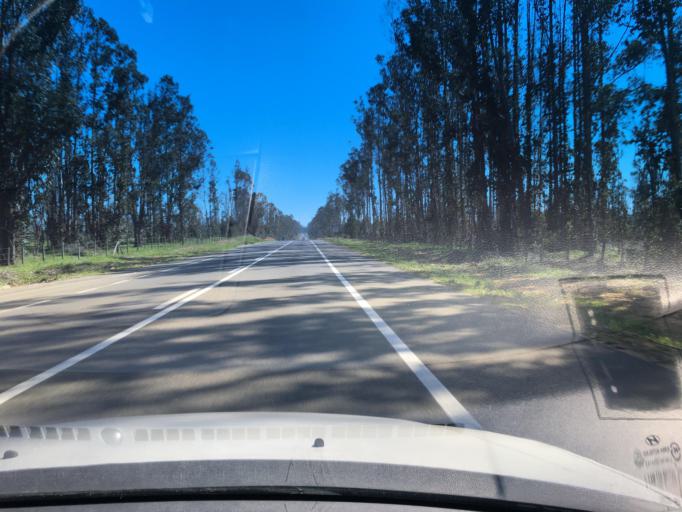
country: CL
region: Valparaiso
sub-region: San Antonio Province
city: El Tabo
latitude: -33.4048
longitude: -71.5676
